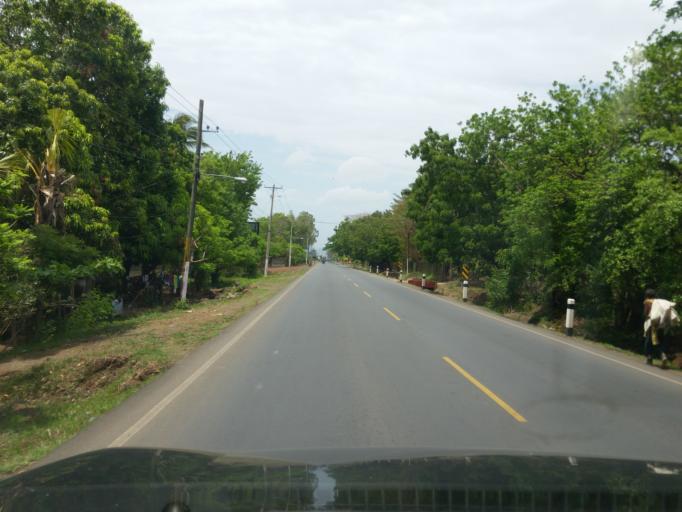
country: NI
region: Granada
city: Nandaime
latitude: 11.7718
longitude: -86.0513
